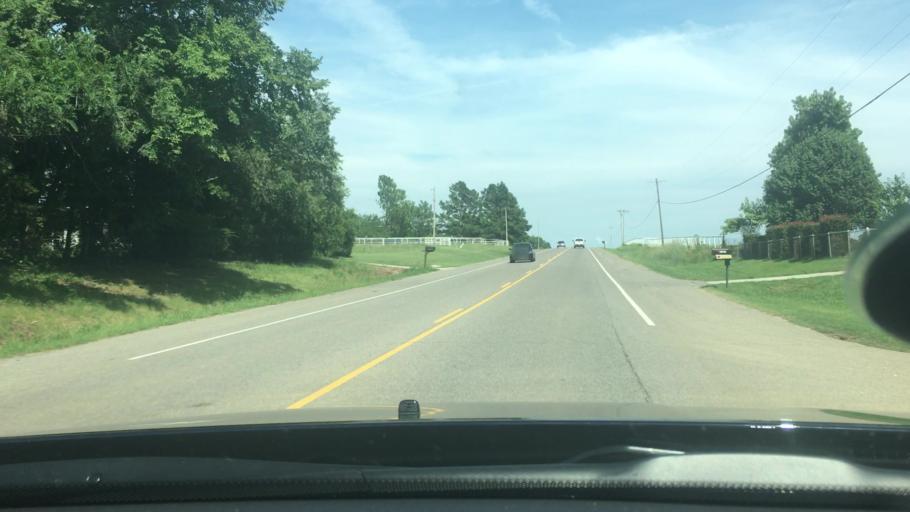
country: US
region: Oklahoma
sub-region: Pottawatomie County
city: Shawnee
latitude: 35.3331
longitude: -96.8249
